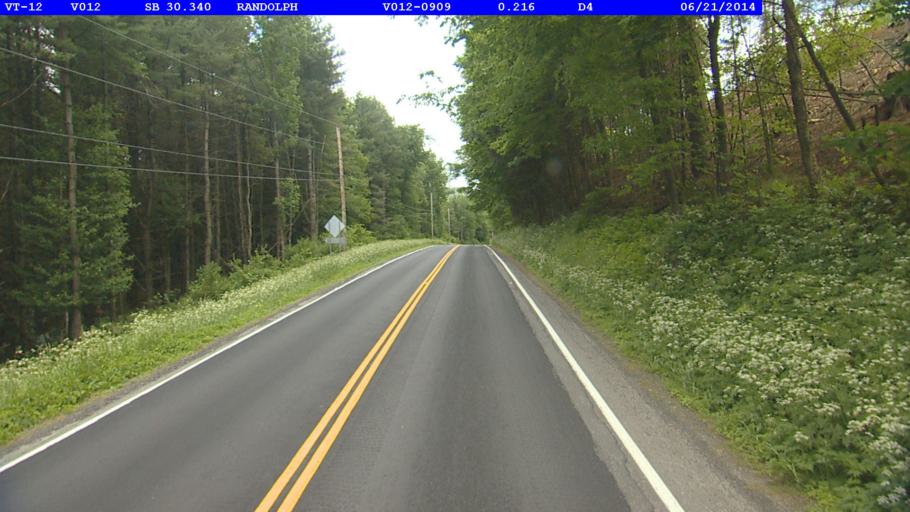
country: US
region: Vermont
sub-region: Orange County
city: Randolph
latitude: 43.8977
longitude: -72.6546
